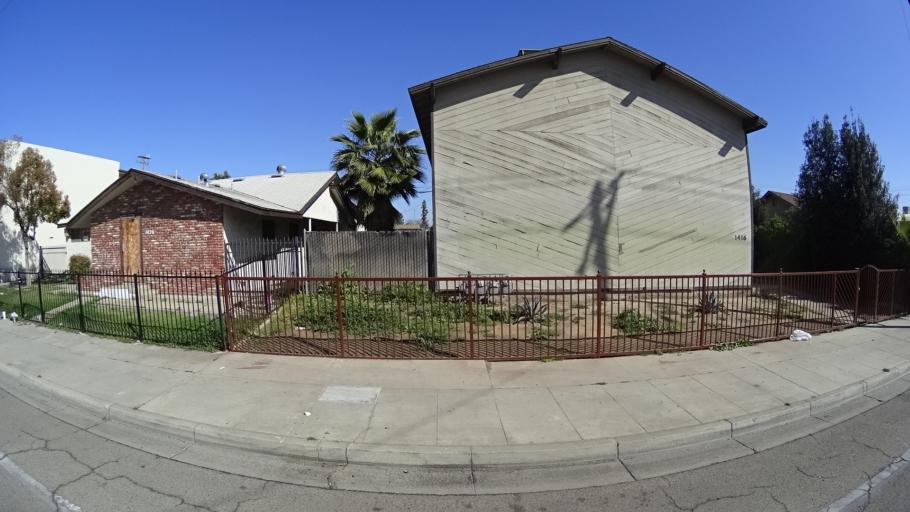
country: US
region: California
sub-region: Fresno County
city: Fresno
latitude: 36.7794
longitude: -119.8280
